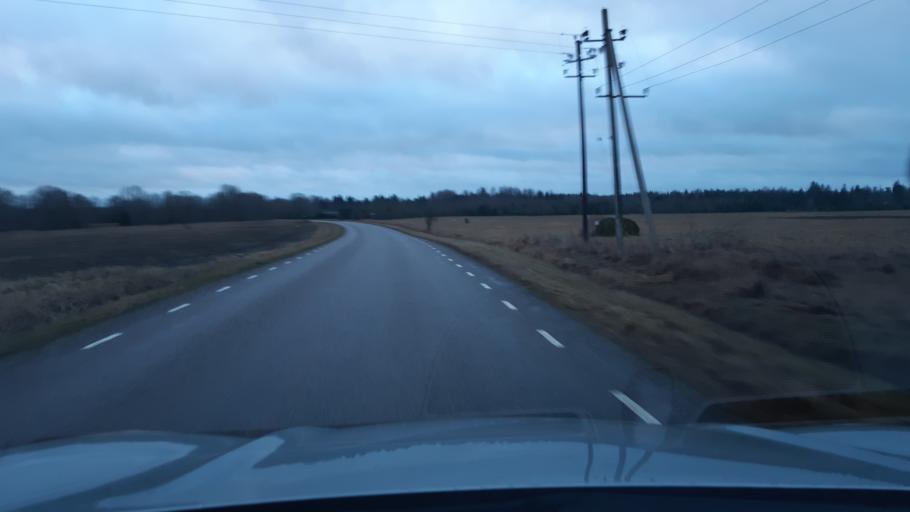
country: EE
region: Raplamaa
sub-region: Kohila vald
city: Kohila
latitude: 59.1554
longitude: 24.6528
